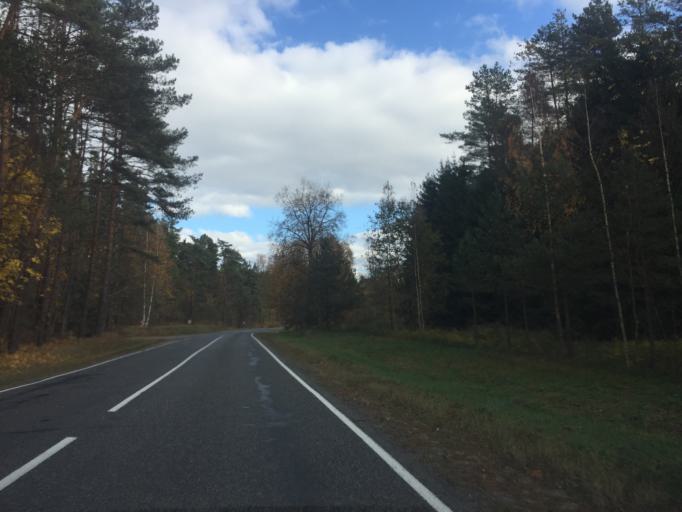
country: BY
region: Minsk
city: Narach
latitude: 54.9460
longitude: 26.5806
